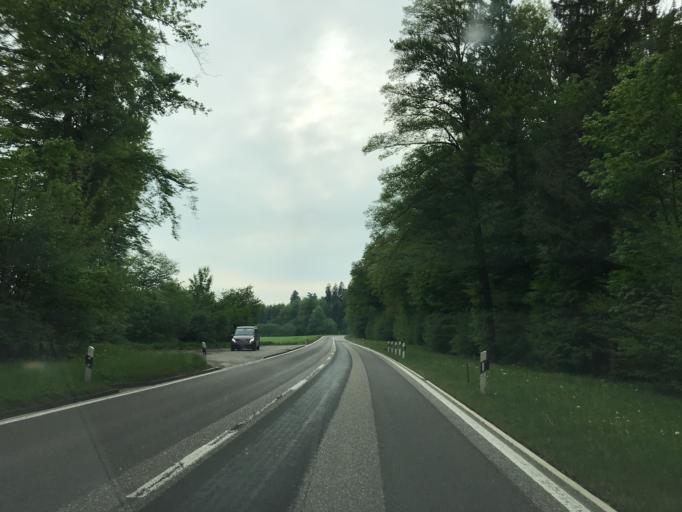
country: CH
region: Bern
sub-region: Oberaargau
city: Aarwangen
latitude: 47.2493
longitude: 7.7441
